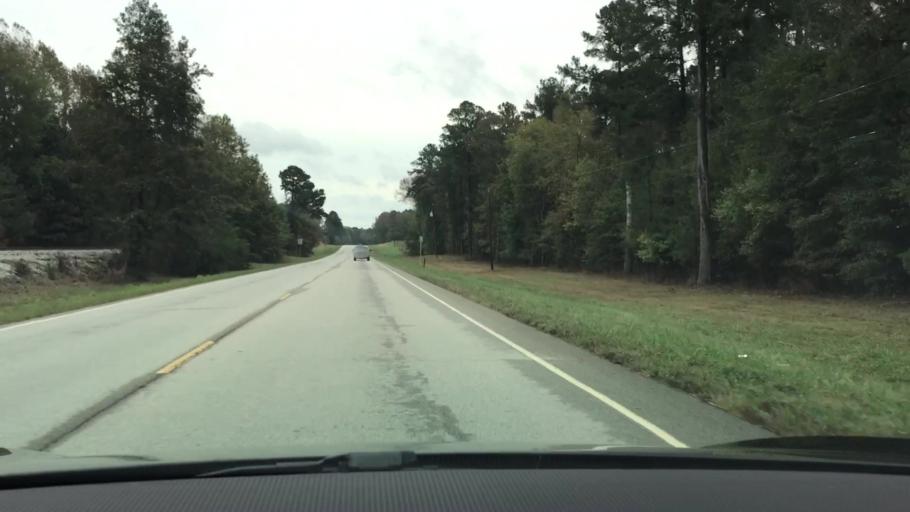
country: US
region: Georgia
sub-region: Warren County
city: Firing Range
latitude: 33.4725
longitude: -82.7239
